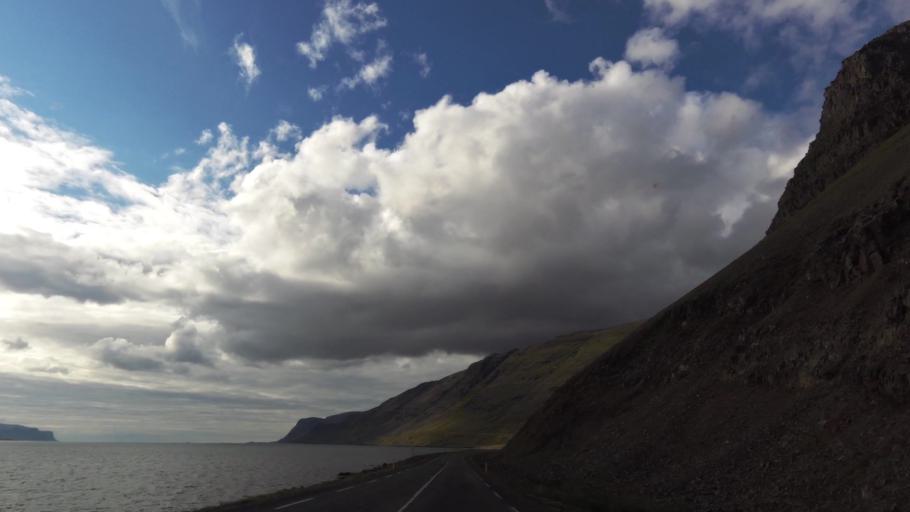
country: IS
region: West
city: Olafsvik
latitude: 65.5460
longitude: -23.8863
